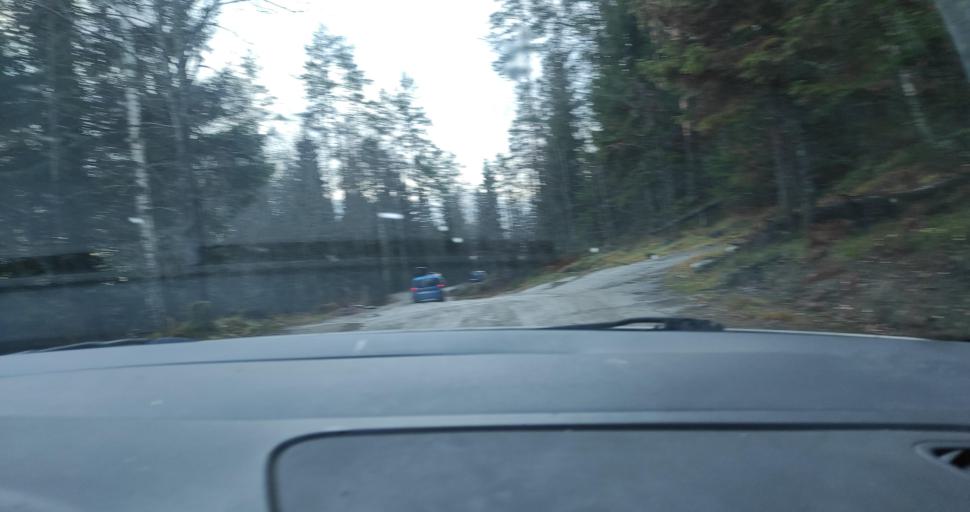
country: RU
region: Republic of Karelia
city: Pitkyaranta
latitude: 61.7466
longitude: 31.3960
